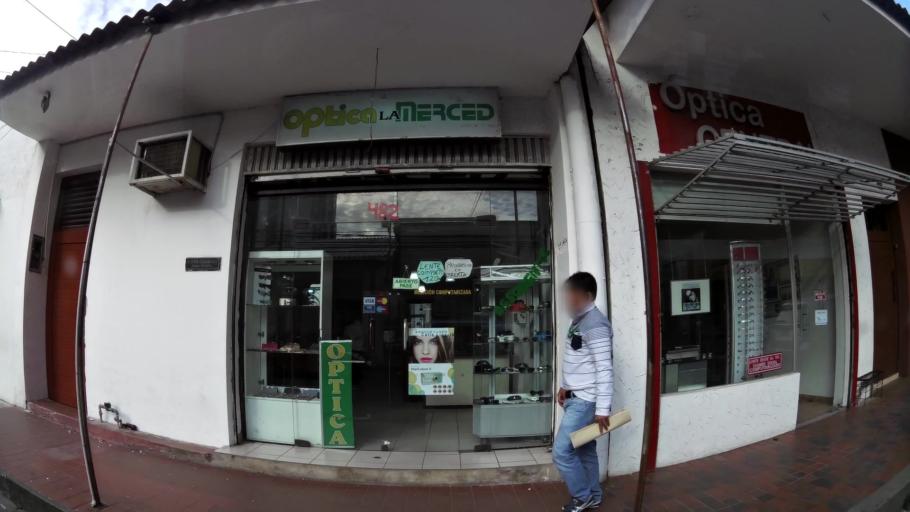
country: BO
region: Santa Cruz
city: Santa Cruz de la Sierra
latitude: -17.7790
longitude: -63.1830
